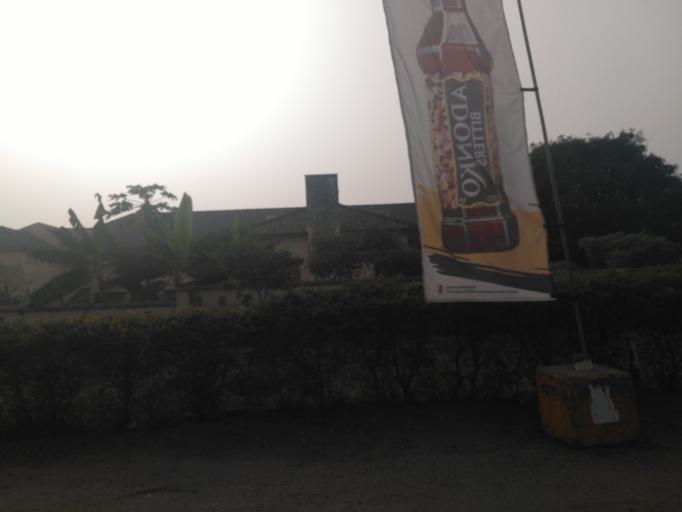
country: GH
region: Ashanti
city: Kumasi
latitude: 6.6860
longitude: -1.6446
